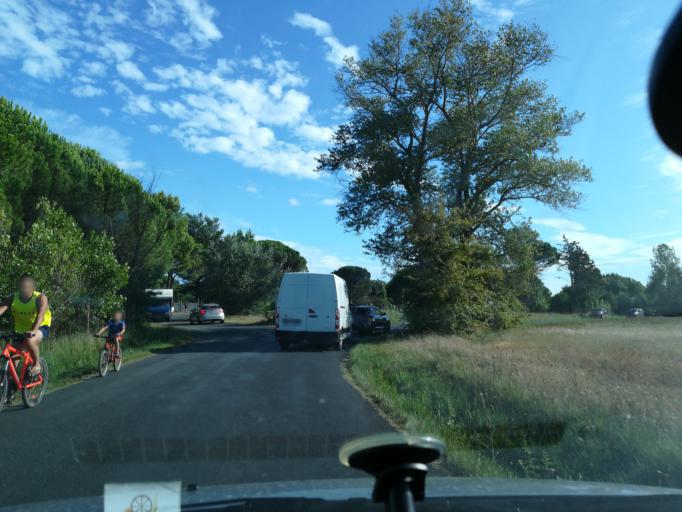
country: FR
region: Languedoc-Roussillon
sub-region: Departement de l'Herault
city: Vias
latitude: 43.2919
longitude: 3.3909
